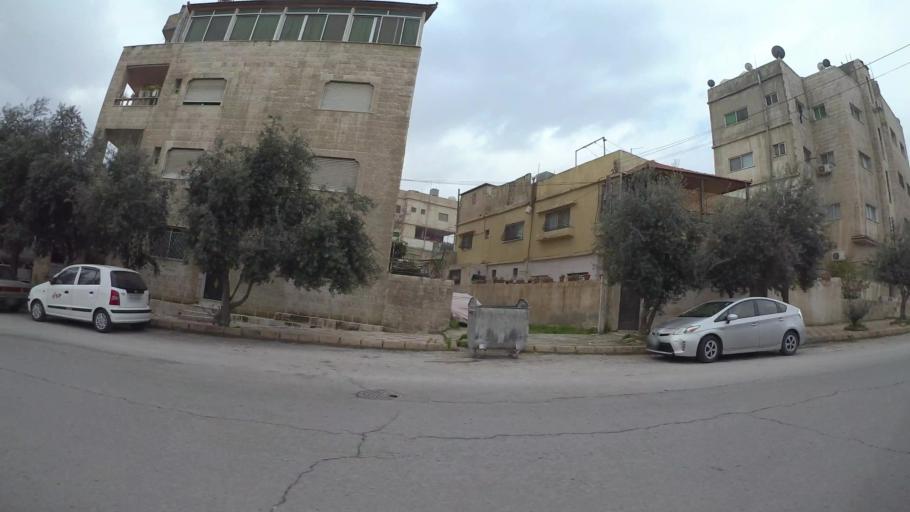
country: JO
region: Amman
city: Amman
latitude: 31.9599
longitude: 35.9423
